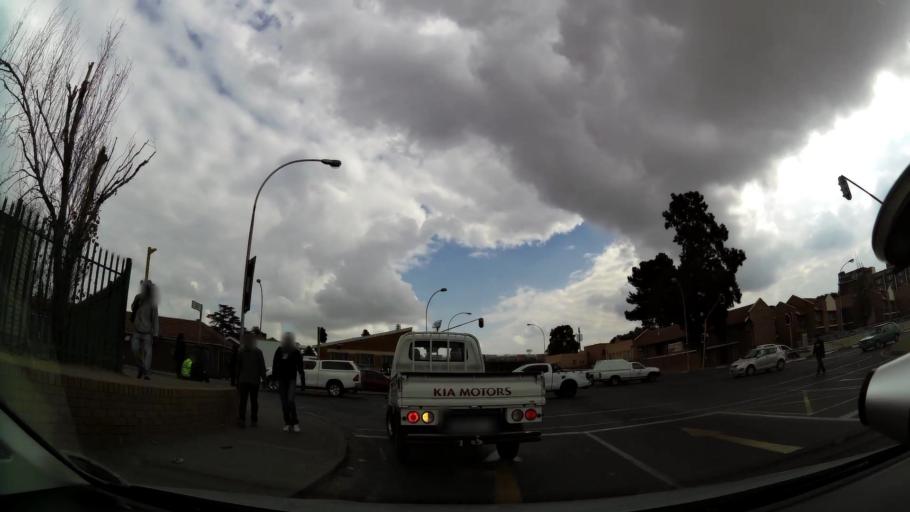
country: ZA
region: Orange Free State
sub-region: Mangaung Metropolitan Municipality
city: Bloemfontein
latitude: -29.1196
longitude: 26.2129
